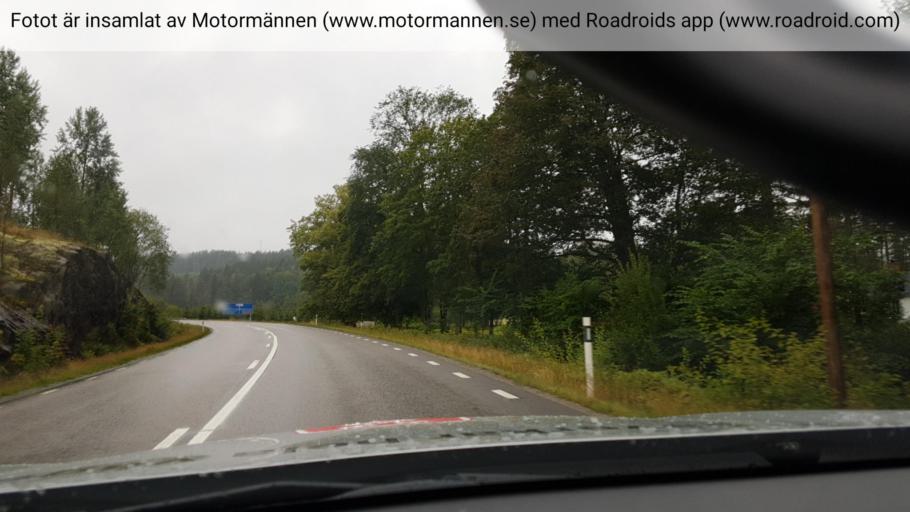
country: SE
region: Vaestra Goetaland
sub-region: Bengtsfors Kommun
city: Bengtsfors
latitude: 59.0210
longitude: 12.2721
